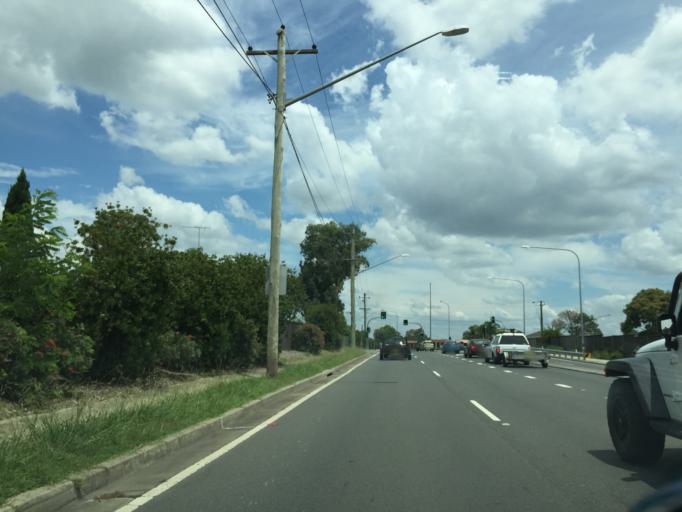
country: AU
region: New South Wales
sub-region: Blacktown
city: Hassall Grove
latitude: -33.7369
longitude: 150.8447
